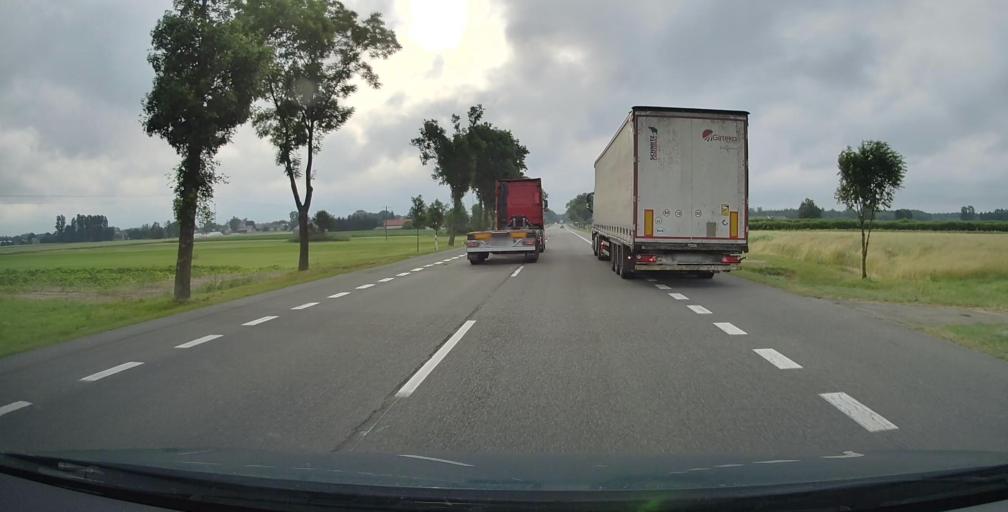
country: PL
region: Lublin Voivodeship
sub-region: Powiat lukowski
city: Trzebieszow
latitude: 52.0575
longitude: 22.6045
